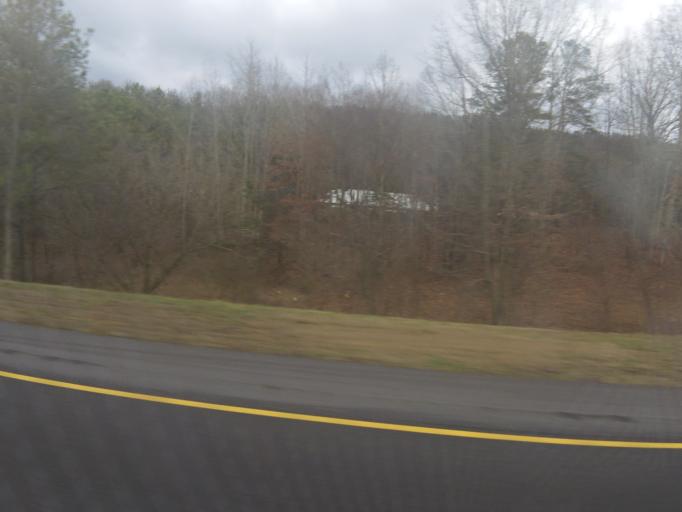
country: US
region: Georgia
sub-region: Whitfield County
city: Varnell
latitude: 34.8433
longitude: -85.0181
